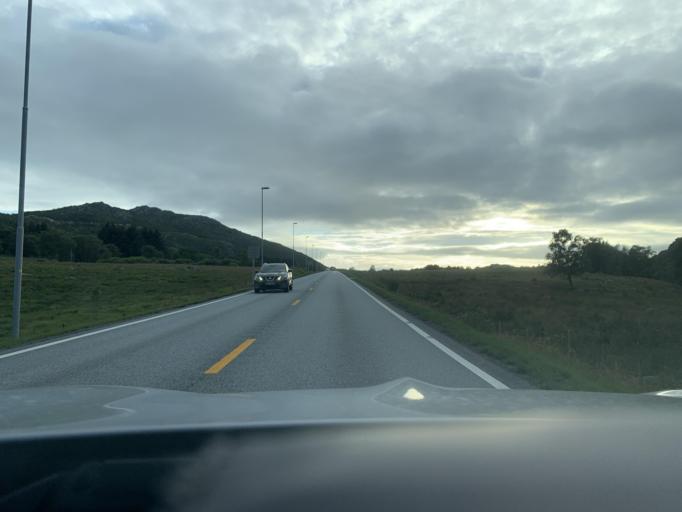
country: NO
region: Rogaland
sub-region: Bjerkreim
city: Vikesa
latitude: 58.6426
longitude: 6.0714
